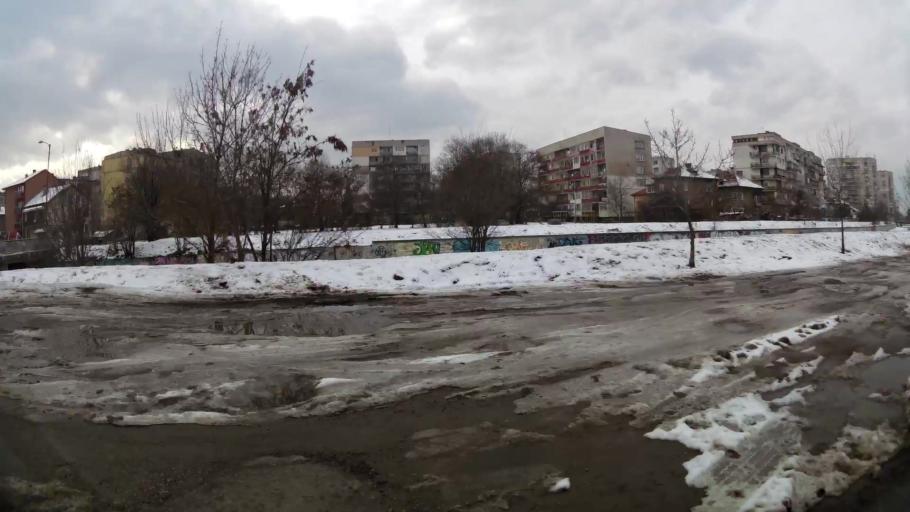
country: BG
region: Sofia-Capital
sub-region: Stolichna Obshtina
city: Sofia
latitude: 42.7037
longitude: 23.3729
